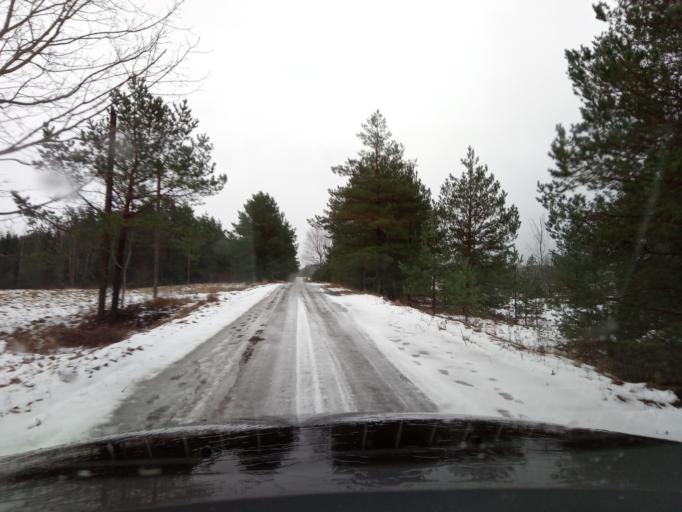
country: LT
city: Svencioneliai
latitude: 55.3465
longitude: 25.8314
